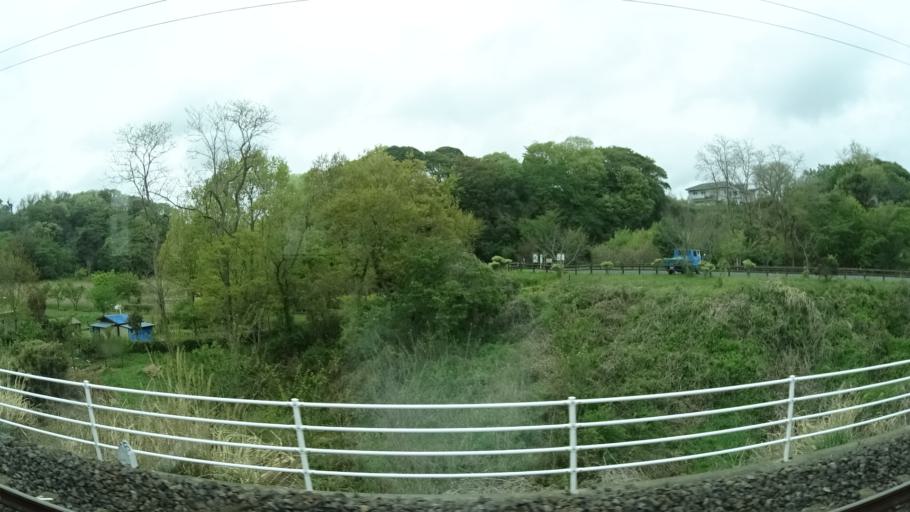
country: JP
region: Ibaraki
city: Funaishikawa
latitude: 36.4997
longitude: 140.6105
